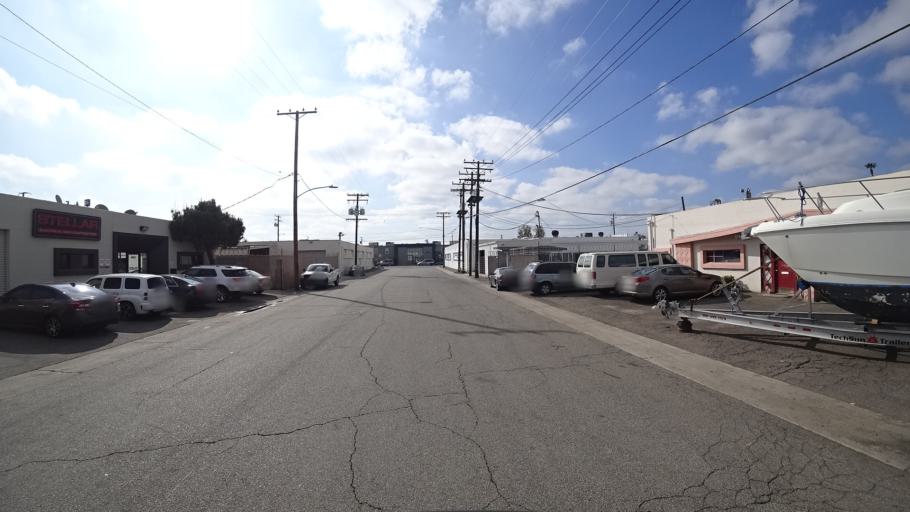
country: US
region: California
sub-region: Orange County
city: Anaheim
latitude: 33.8263
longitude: -117.9001
